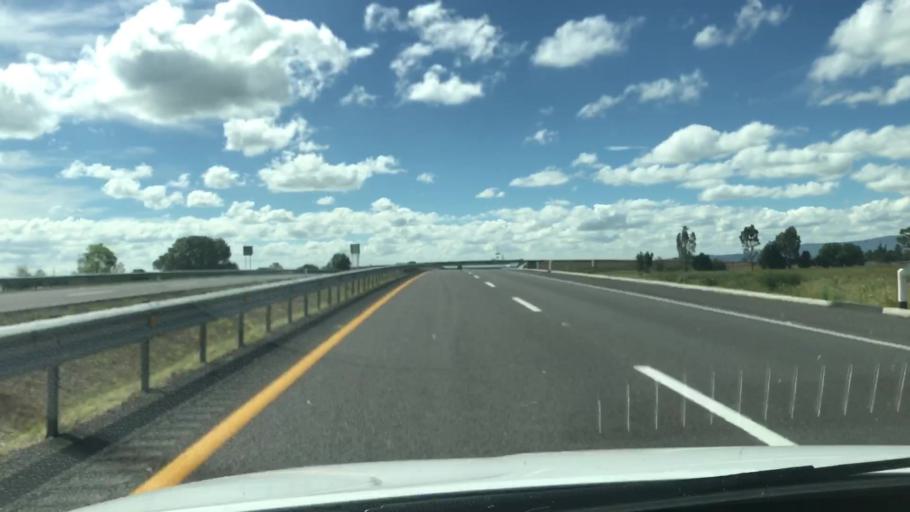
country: MX
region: Guanajuato
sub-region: Silao de la Victoria
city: La Aldea
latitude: 20.9133
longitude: -101.4923
